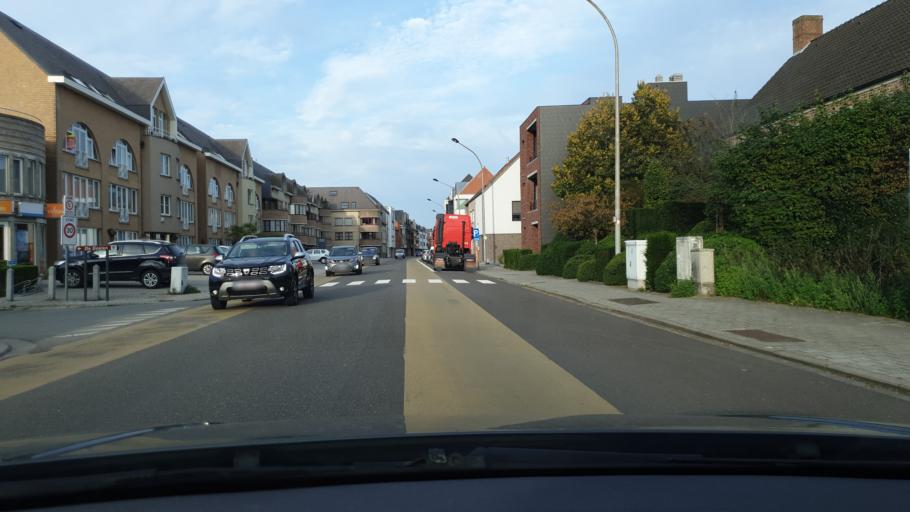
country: BE
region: Flanders
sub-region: Provincie Antwerpen
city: Geel
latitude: 51.1590
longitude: 4.9961
